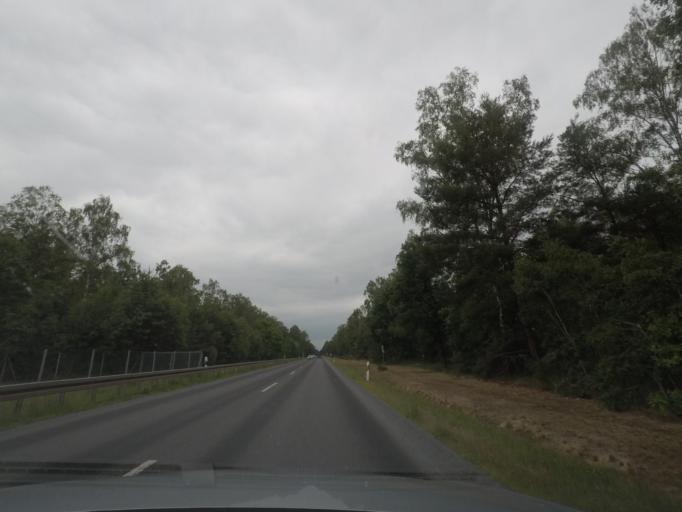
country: DE
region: Saxony-Anhalt
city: Colbitz
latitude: 52.3547
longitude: 11.5475
